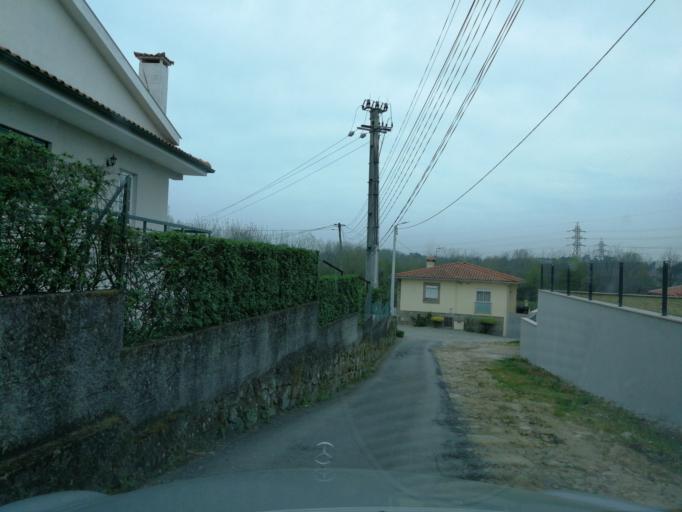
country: PT
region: Braga
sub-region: Braga
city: Braga
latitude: 41.5735
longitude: -8.4337
